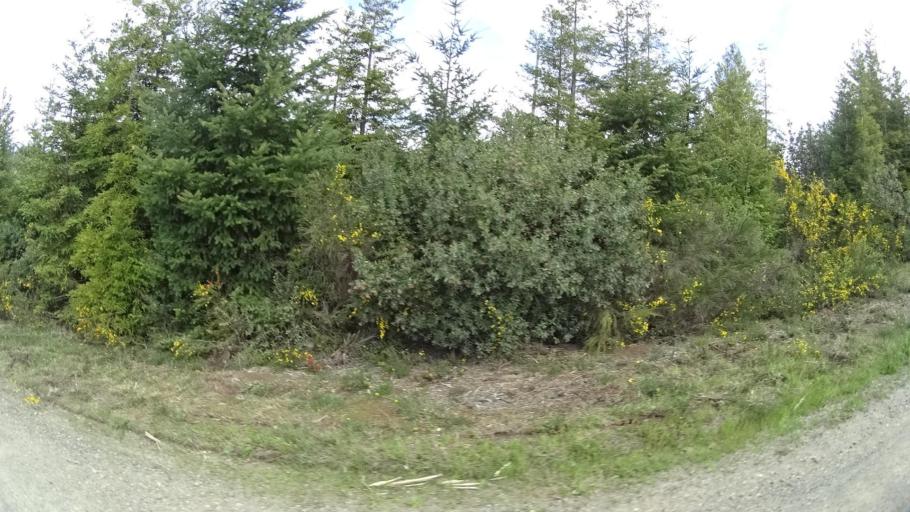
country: US
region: California
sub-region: Humboldt County
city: Blue Lake
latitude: 40.7717
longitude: -123.9608
